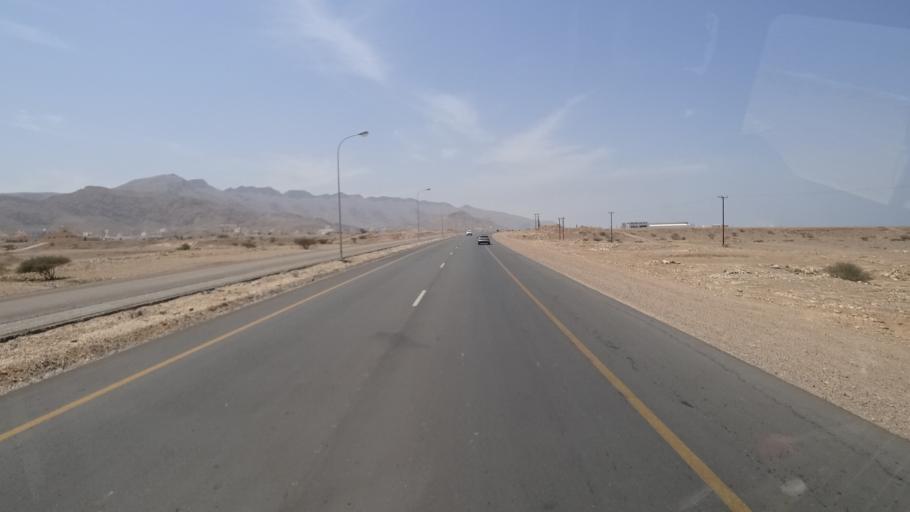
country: OM
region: Ash Sharqiyah
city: Sur
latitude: 22.5874
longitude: 59.4423
